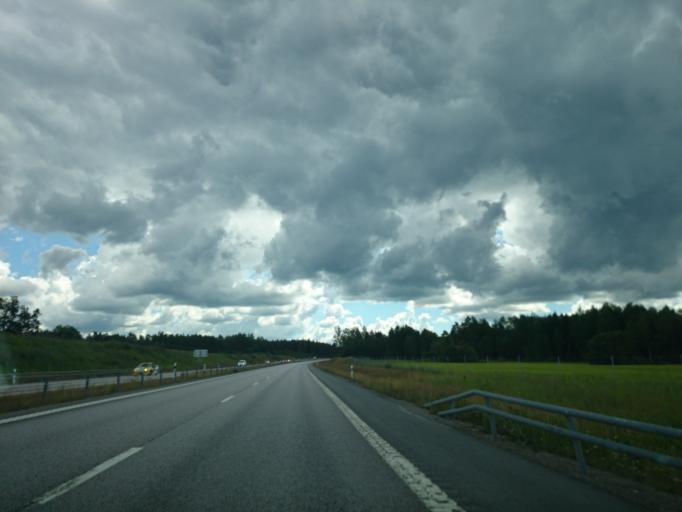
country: SE
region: Uppsala
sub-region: Tierps Kommun
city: Tierp
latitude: 60.3211
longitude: 17.5151
